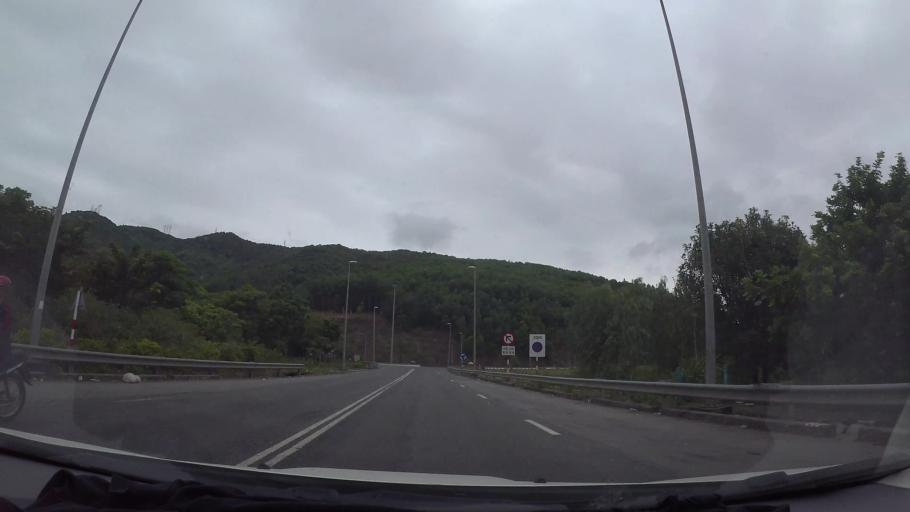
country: VN
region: Da Nang
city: Lien Chieu
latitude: 16.1304
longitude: 108.1060
